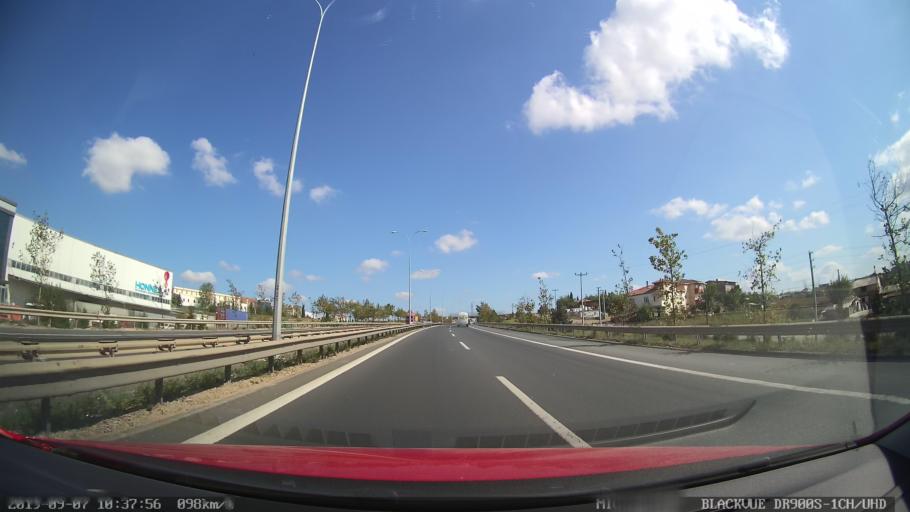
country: TR
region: Kocaeli
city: Balcik
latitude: 40.8545
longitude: 29.3752
